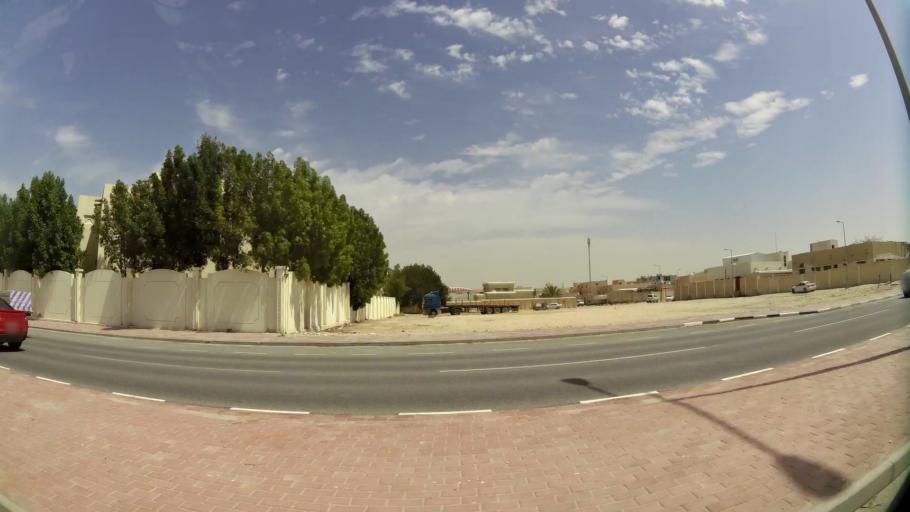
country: QA
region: Baladiyat ar Rayyan
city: Ar Rayyan
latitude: 25.2919
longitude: 51.4066
